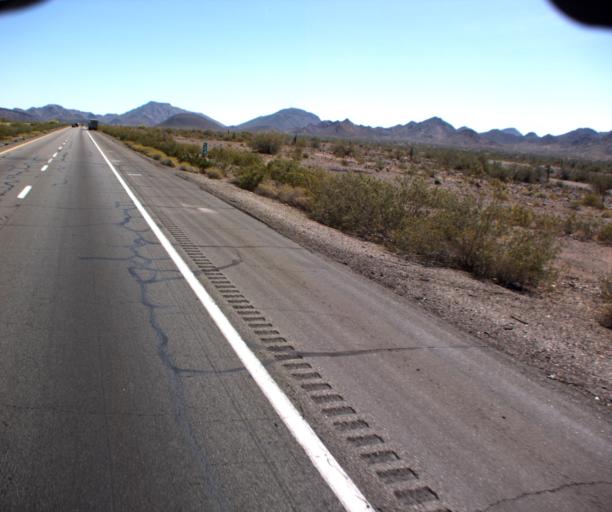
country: US
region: Arizona
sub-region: La Paz County
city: Quartzsite
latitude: 33.6751
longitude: -114.1303
